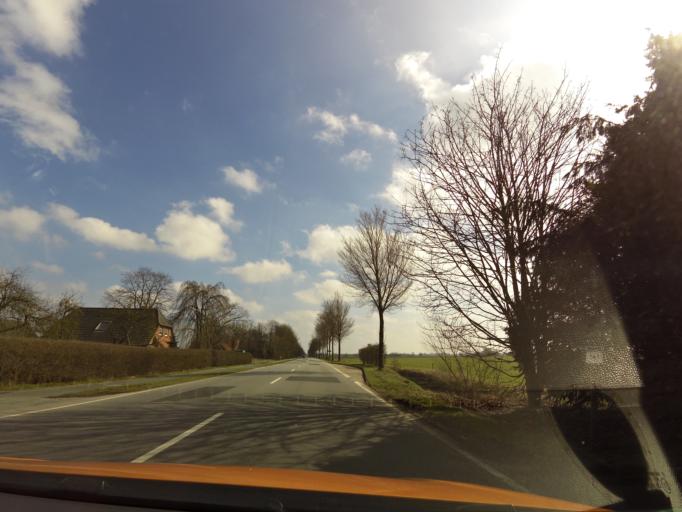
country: DE
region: Lower Saxony
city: Varel
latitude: 53.3869
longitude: 8.2077
